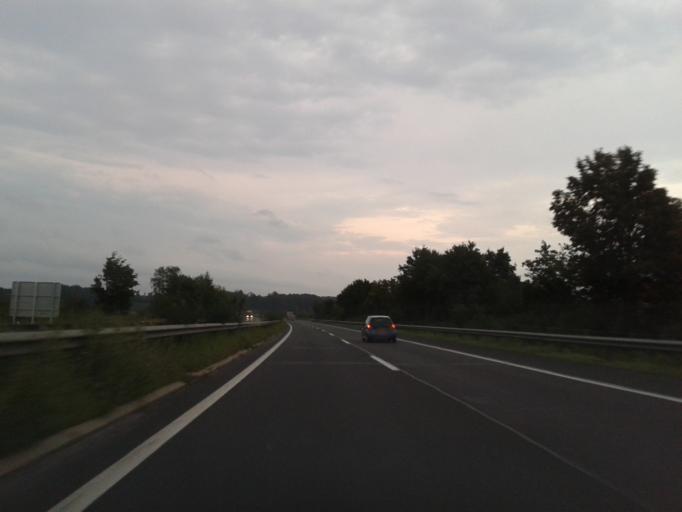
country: AT
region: Styria
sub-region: Politischer Bezirk Hartberg-Fuerstenfeld
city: Hainersdorf
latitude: 47.0873
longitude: 15.9746
